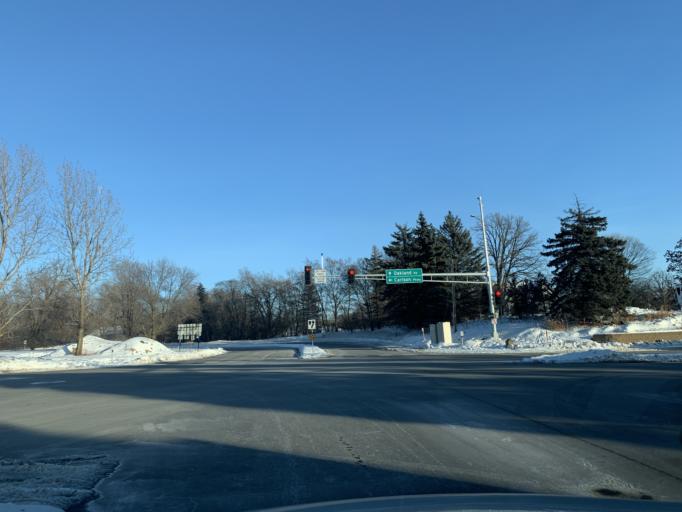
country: US
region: Minnesota
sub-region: Hennepin County
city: Wayzata
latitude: 44.9697
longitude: -93.4701
